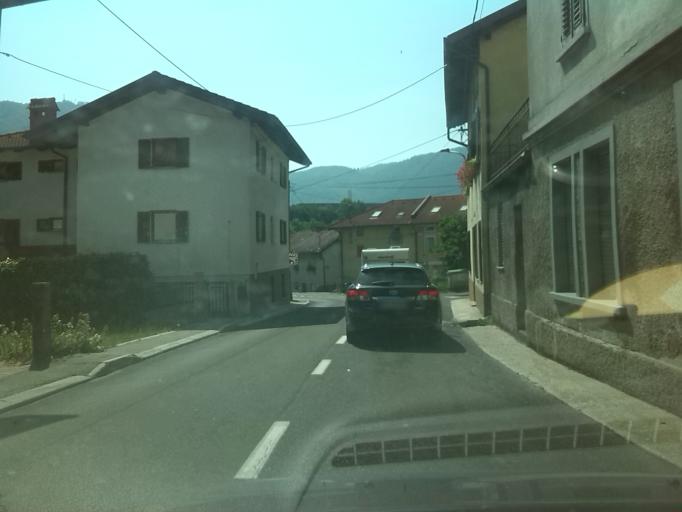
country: SI
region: Tolmin
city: Tolmin
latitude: 46.1847
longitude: 13.7388
